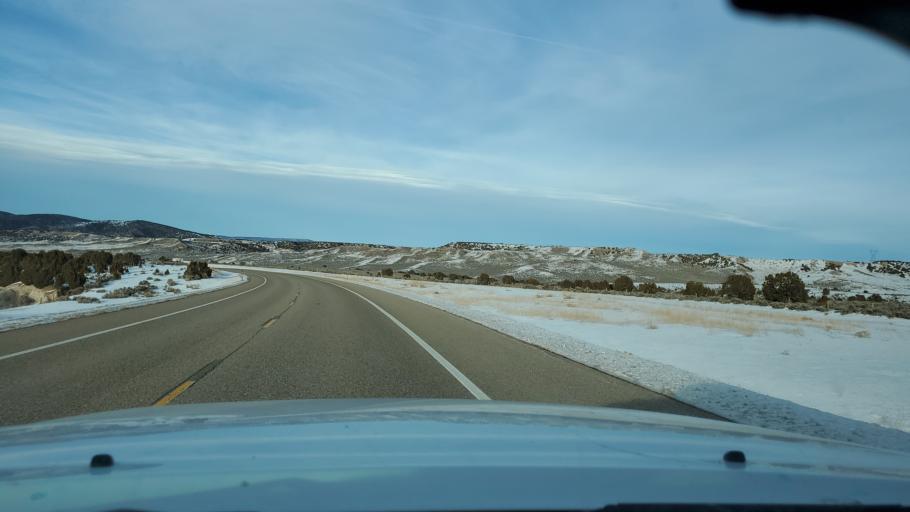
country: US
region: Colorado
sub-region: Rio Blanco County
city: Rangely
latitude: 40.3886
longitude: -108.3490
